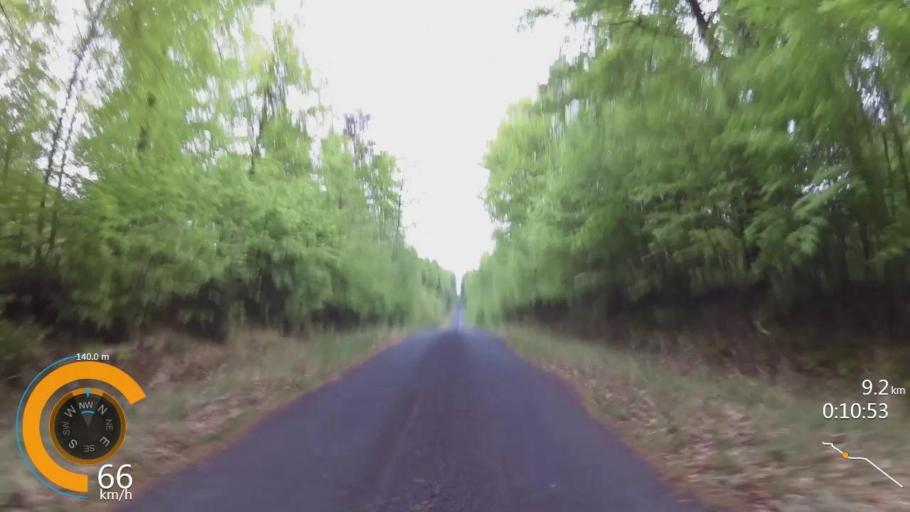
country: PL
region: West Pomeranian Voivodeship
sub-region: Powiat drawski
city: Wierzchowo
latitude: 53.5088
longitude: 16.1198
